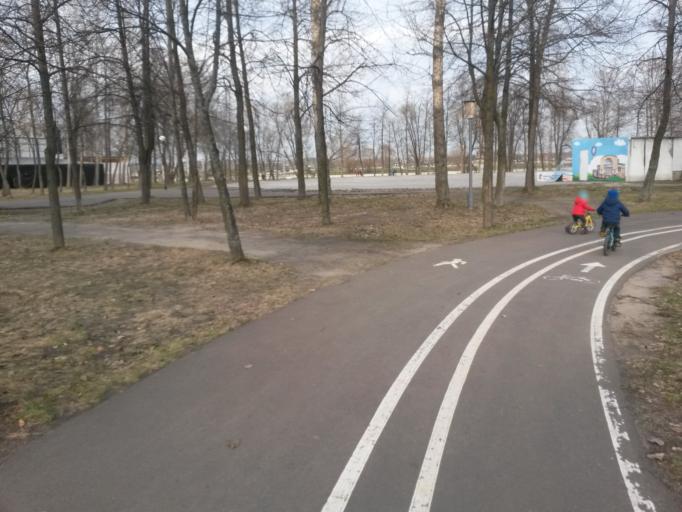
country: RU
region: Jaroslavl
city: Yaroslavl
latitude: 57.6171
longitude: 39.8999
